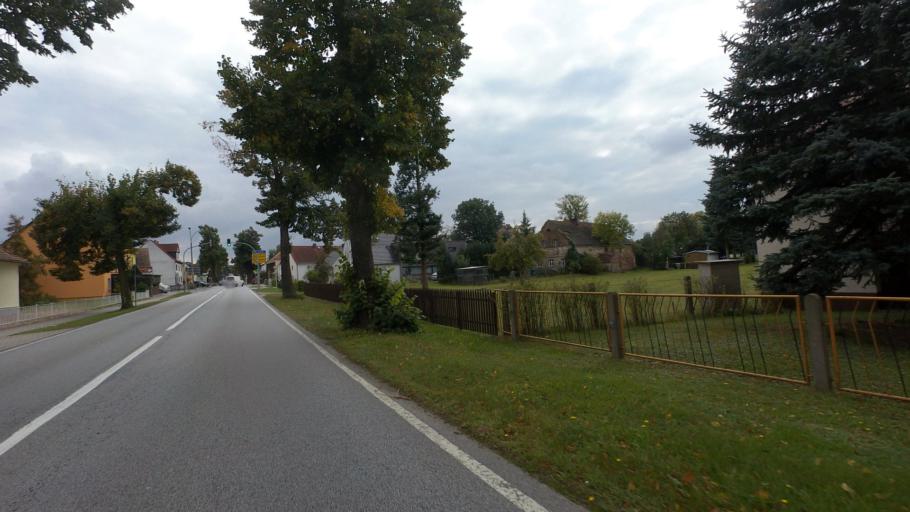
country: DE
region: Saxony
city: Konigswartha
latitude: 51.3713
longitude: 14.3074
